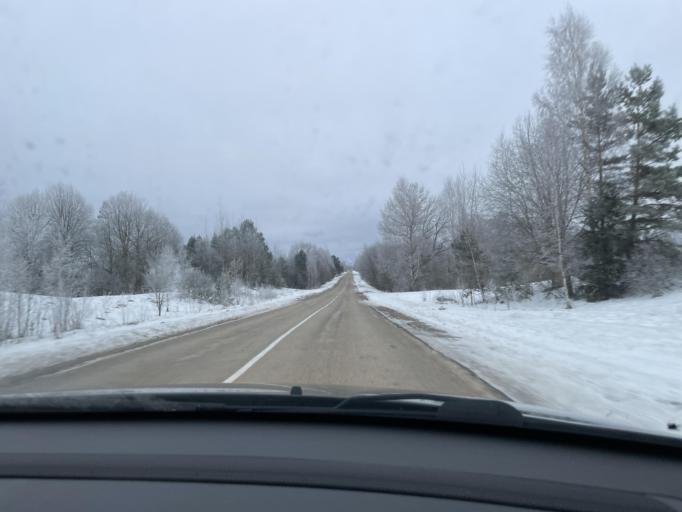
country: LV
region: Rezekne
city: Rezekne
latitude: 56.4379
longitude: 27.5253
